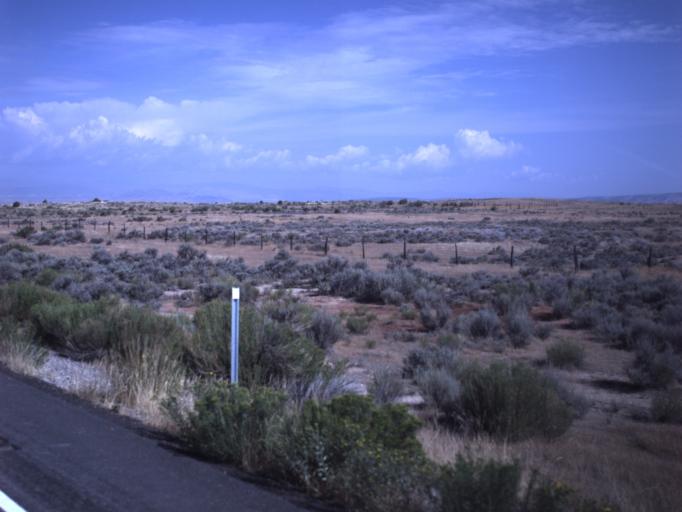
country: US
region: Utah
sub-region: Uintah County
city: Naples
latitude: 40.3300
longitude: -109.2779
